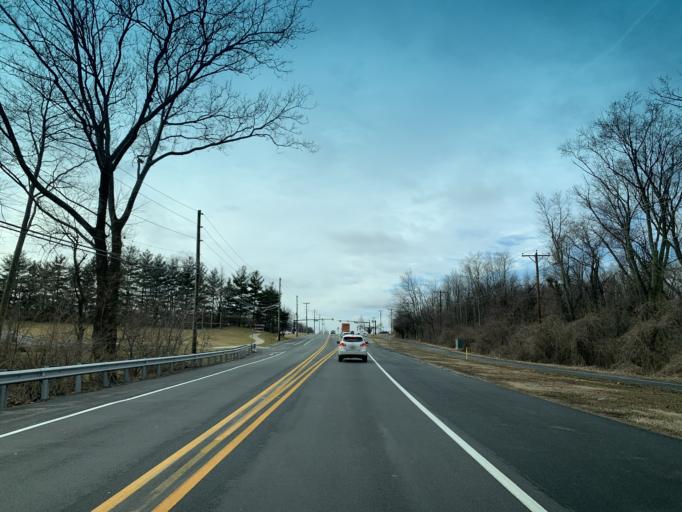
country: US
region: Delaware
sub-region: New Castle County
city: Wilmington Manor
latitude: 39.6650
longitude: -75.5954
